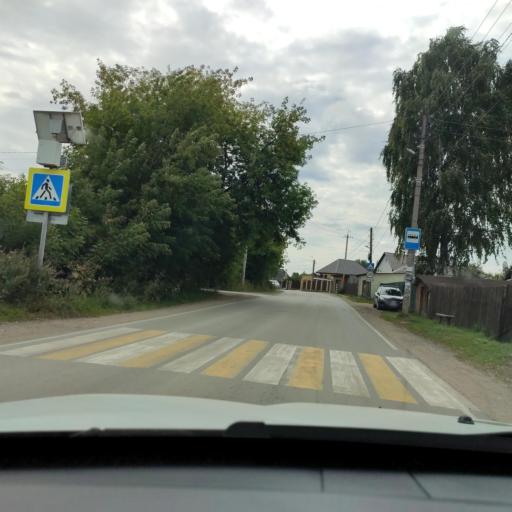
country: RU
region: Perm
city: Krasnokamsk
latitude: 58.0787
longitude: 55.7961
